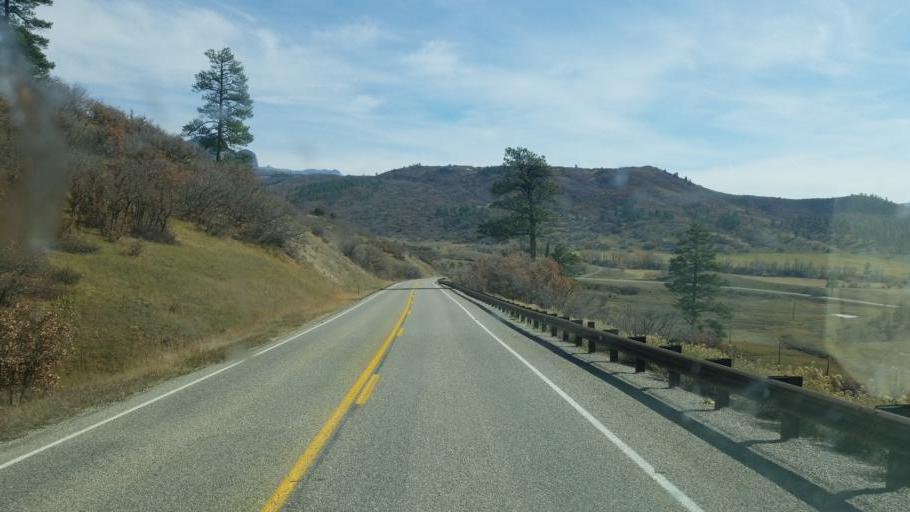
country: US
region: New Mexico
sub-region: Rio Arriba County
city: Dulce
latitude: 37.0739
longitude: -106.8331
